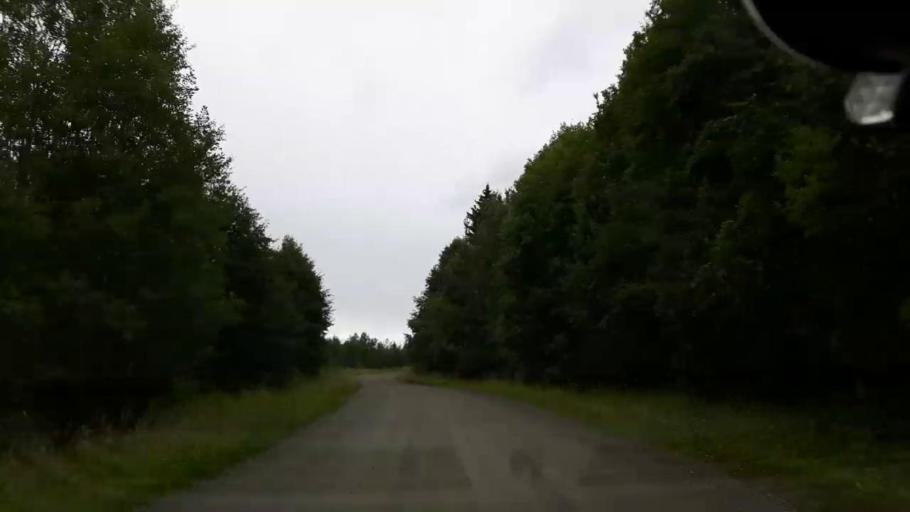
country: SE
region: Jaemtland
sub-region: Bergs Kommun
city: Hoverberg
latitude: 62.7983
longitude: 14.4734
